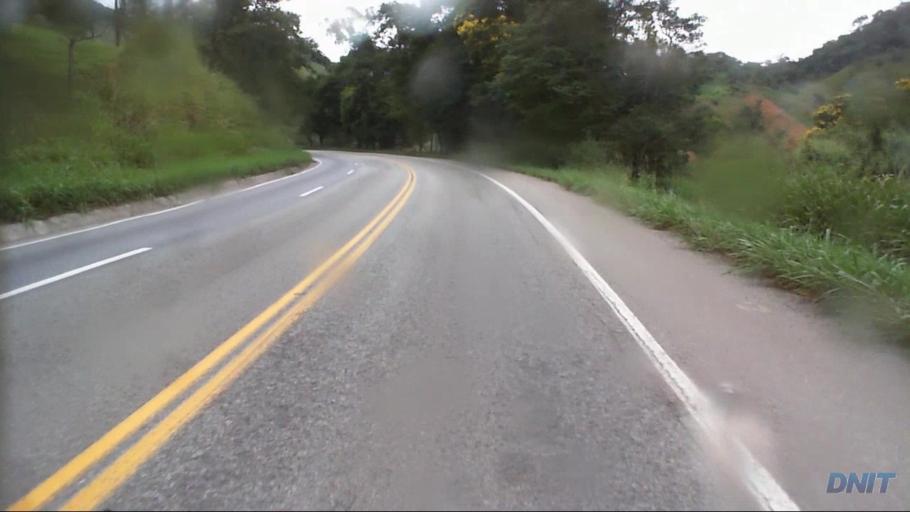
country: BR
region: Minas Gerais
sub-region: Nova Era
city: Nova Era
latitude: -19.7092
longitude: -43.0003
